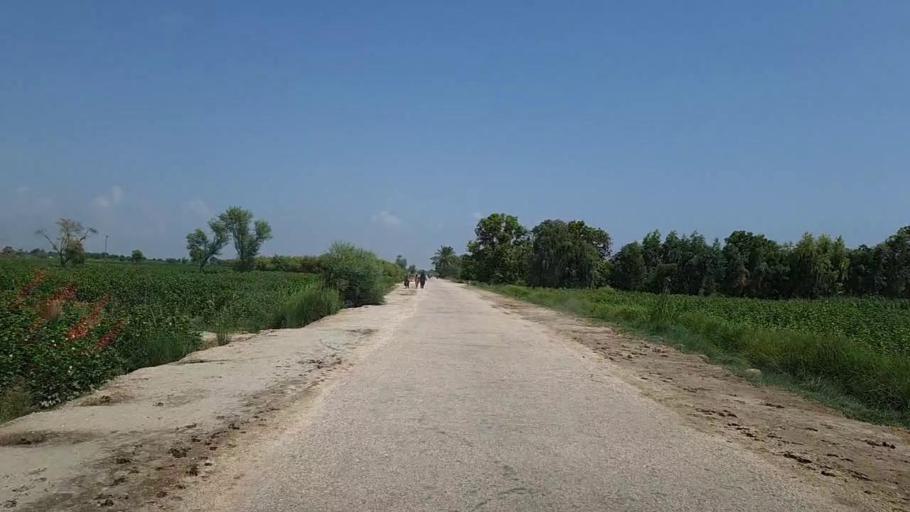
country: PK
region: Sindh
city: Bhiria
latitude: 26.8949
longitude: 68.2218
